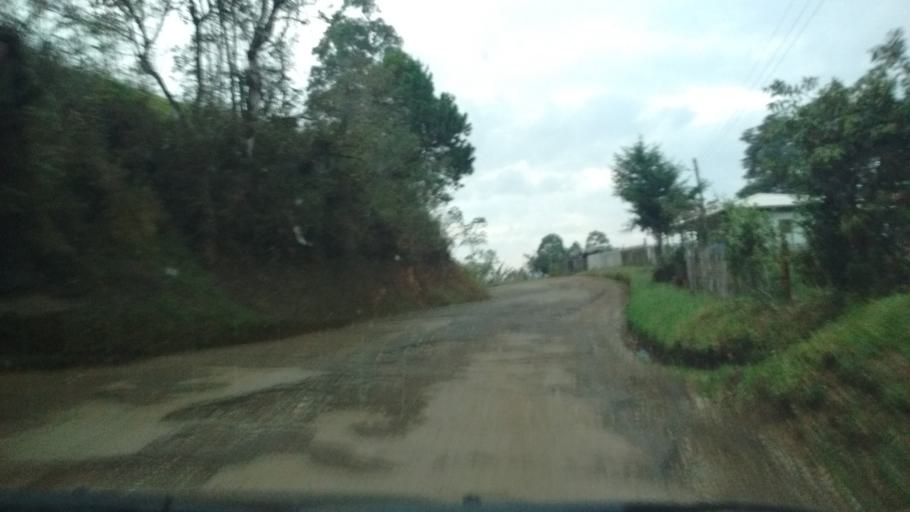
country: CO
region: Cauca
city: Lopez
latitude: 2.3784
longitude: -76.7152
